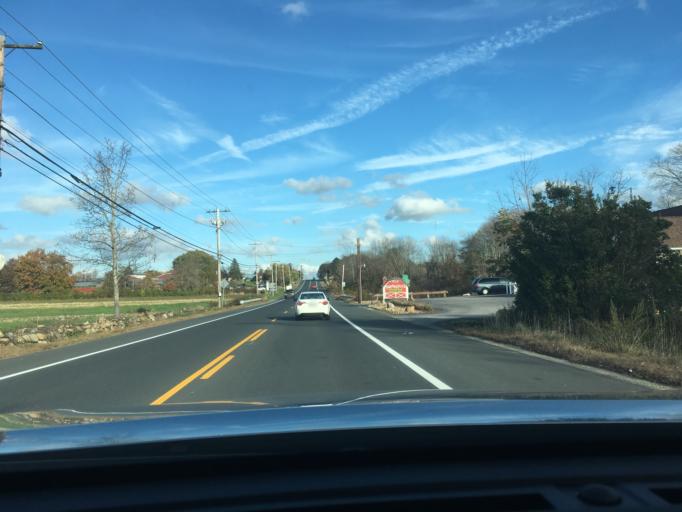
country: US
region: Rhode Island
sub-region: Providence County
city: Johnston
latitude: 41.7918
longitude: -71.5507
